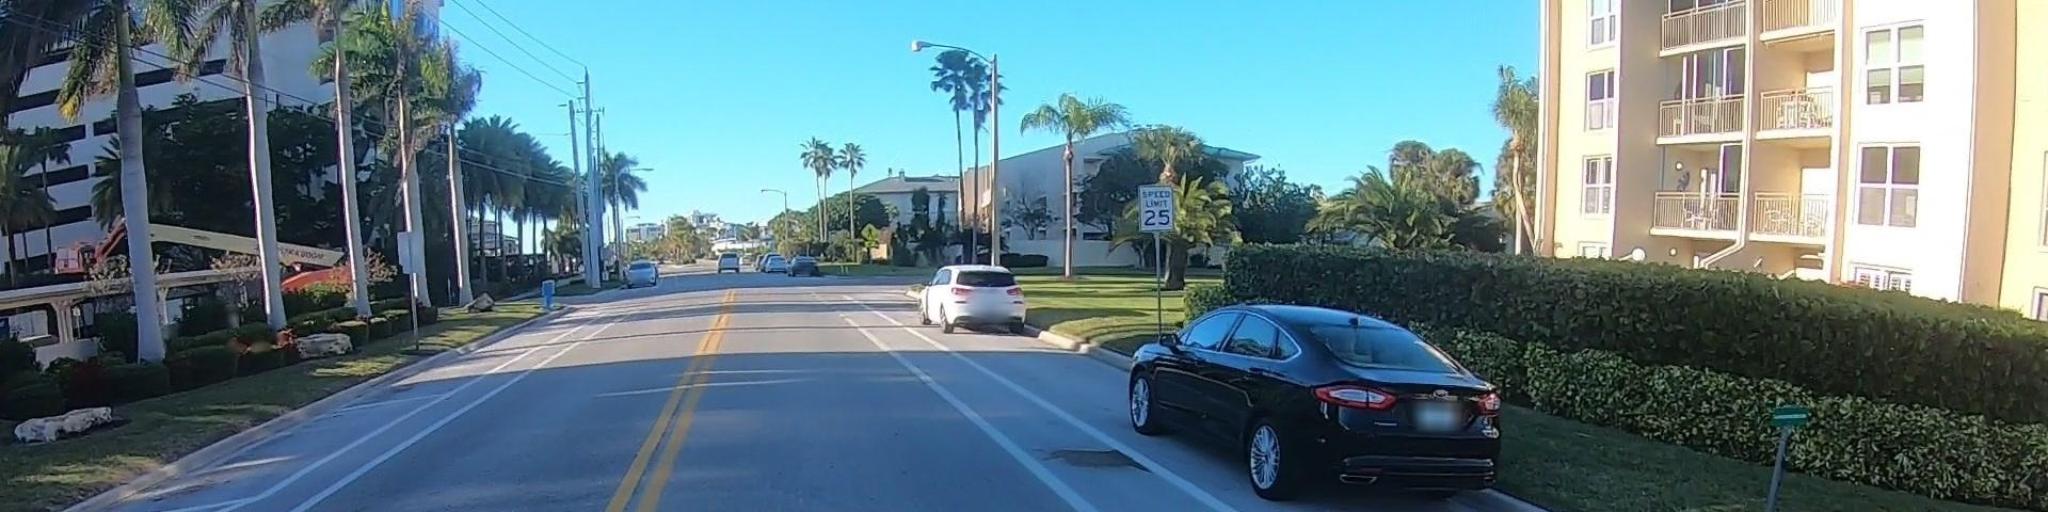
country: US
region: Florida
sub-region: Sarasota County
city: Siesta Key
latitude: 27.3096
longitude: -82.5736
